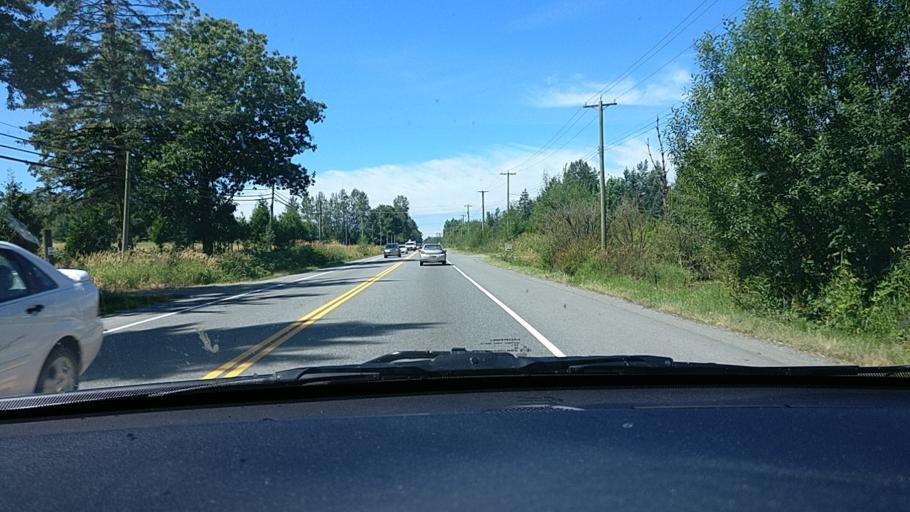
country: CA
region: British Columbia
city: Aldergrove
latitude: 49.0575
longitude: -122.4099
